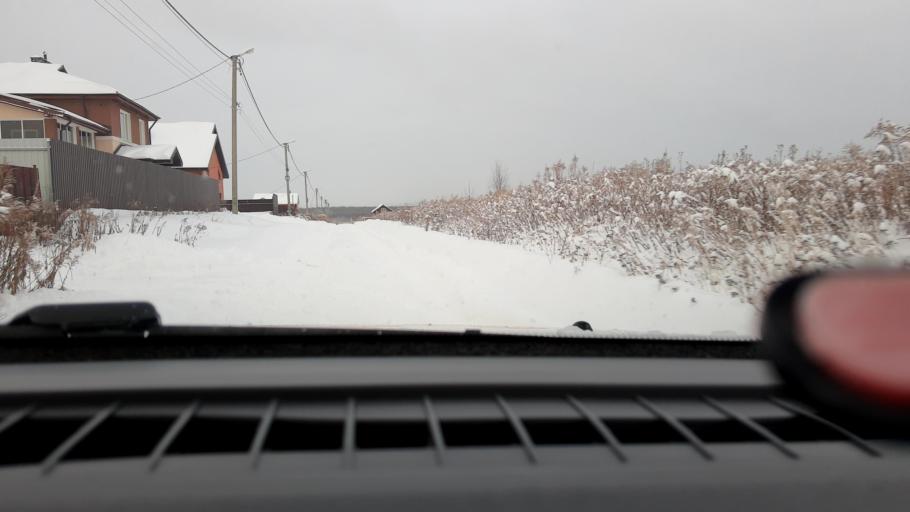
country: RU
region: Nizjnij Novgorod
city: Afonino
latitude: 56.1283
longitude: 43.9941
